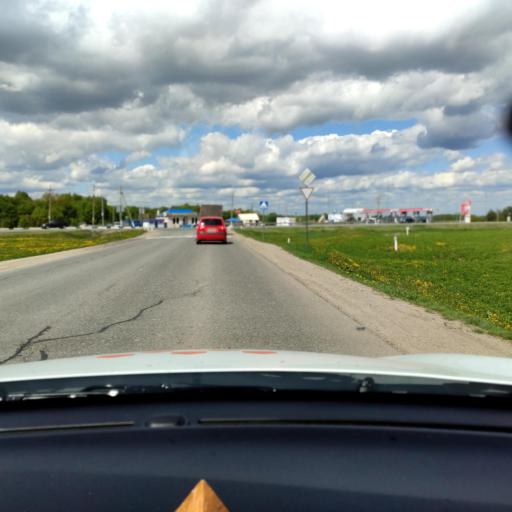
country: RU
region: Tatarstan
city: Verkhniy Uslon
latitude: 55.6587
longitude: 48.8583
